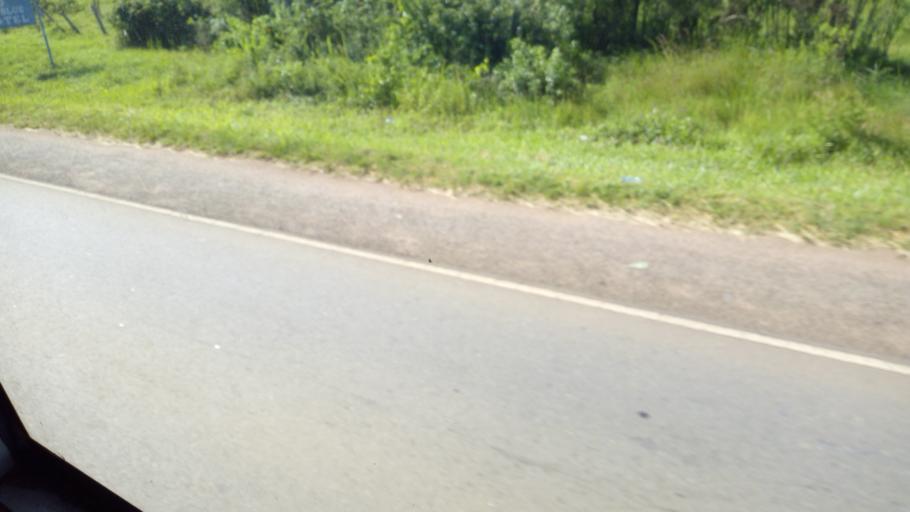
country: UG
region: Central Region
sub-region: Lyantonde District
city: Lyantonde
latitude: -0.4015
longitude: 31.1639
